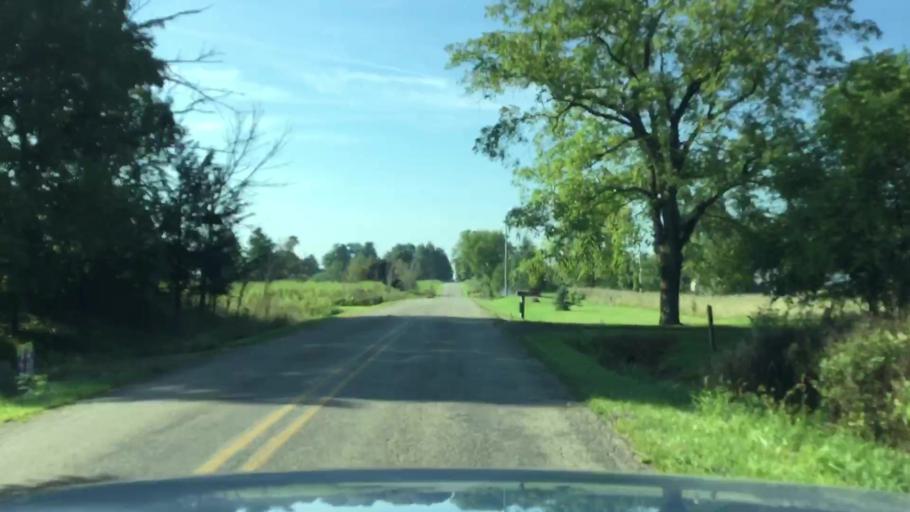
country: US
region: Michigan
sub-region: Lenawee County
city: Hudson
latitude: 41.8915
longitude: -84.4203
